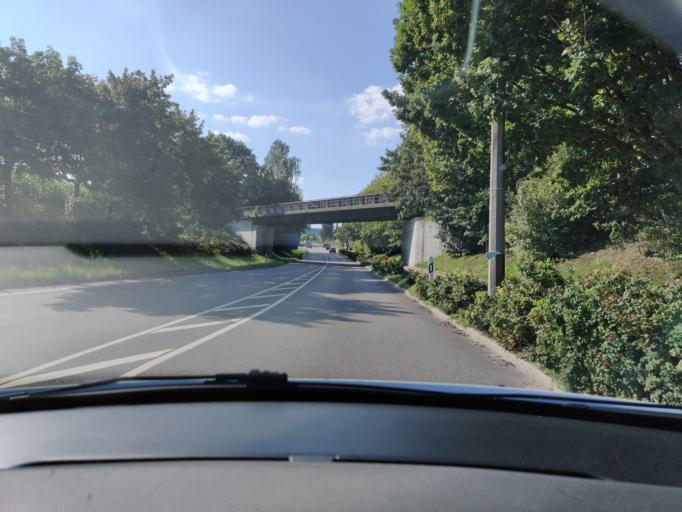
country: DE
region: Bavaria
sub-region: Upper Palatinate
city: Wackersdorf
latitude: 49.3170
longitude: 12.1475
